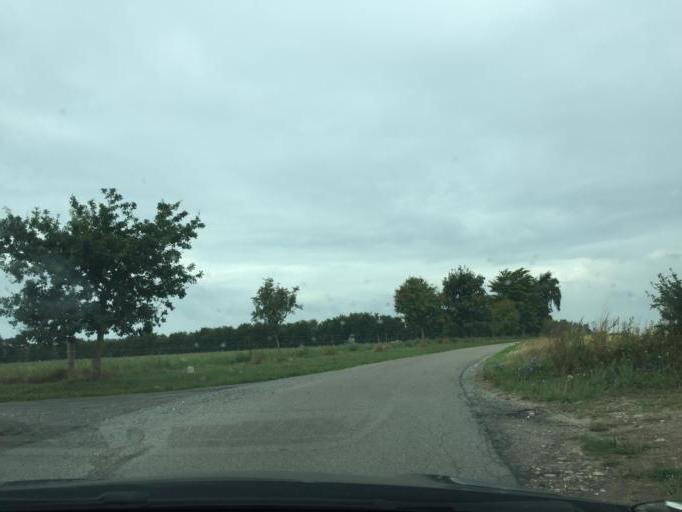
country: DK
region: South Denmark
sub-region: Assens Kommune
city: Harby
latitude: 55.2066
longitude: 10.0124
